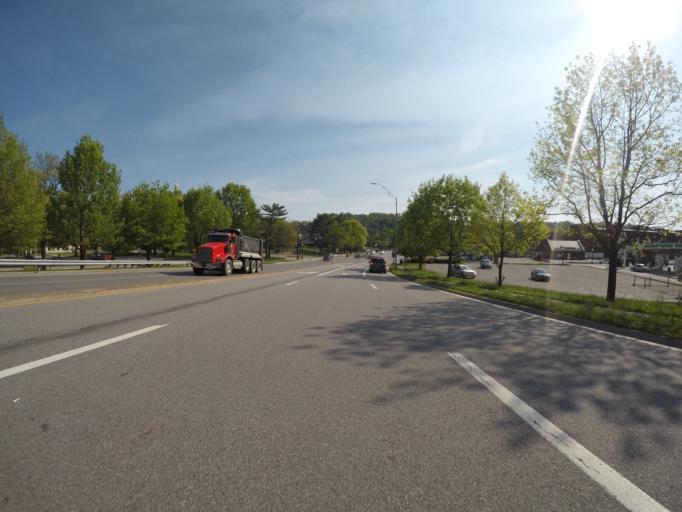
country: US
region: West Virginia
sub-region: Kanawha County
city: Charleston
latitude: 38.3399
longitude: -81.6138
